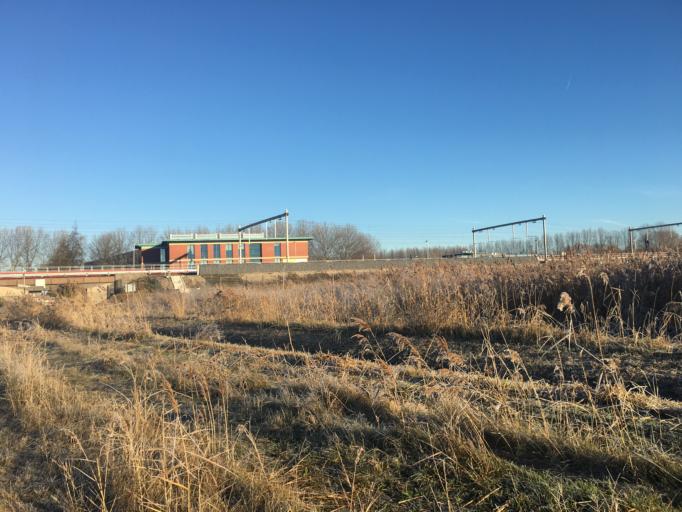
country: NL
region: Flevoland
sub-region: Gemeente Almere
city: Almere Stad
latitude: 52.3754
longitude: 5.2271
